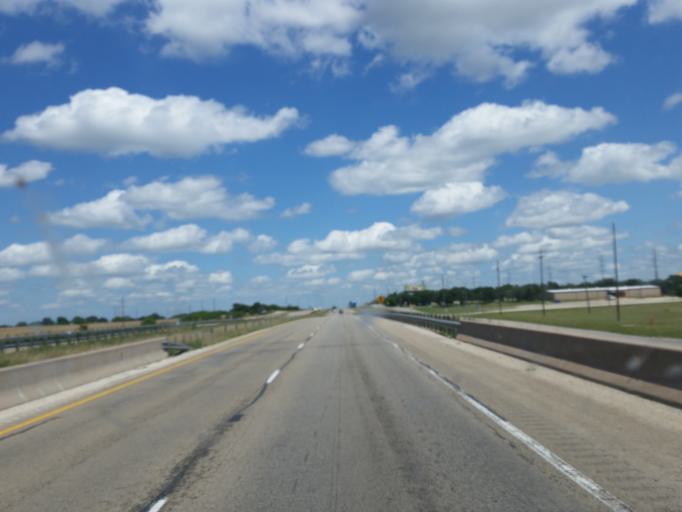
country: US
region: Texas
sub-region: Callahan County
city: Clyde
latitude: 32.4182
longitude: -99.5257
